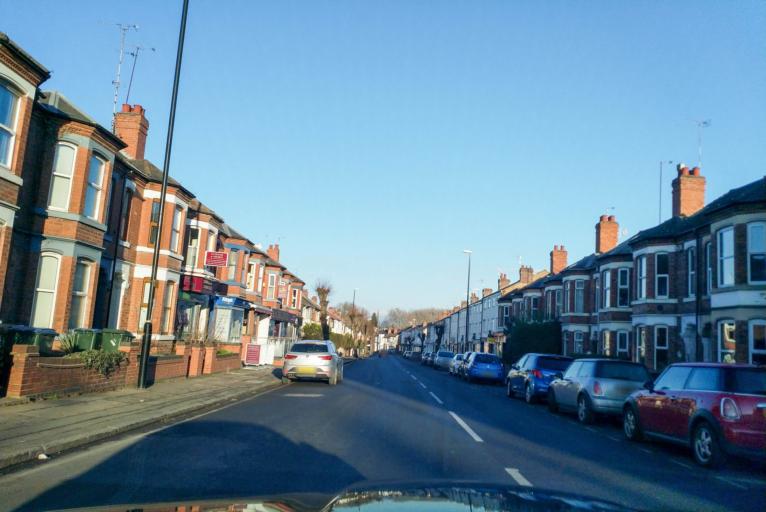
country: GB
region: England
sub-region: Coventry
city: Coventry
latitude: 52.4001
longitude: -1.5300
